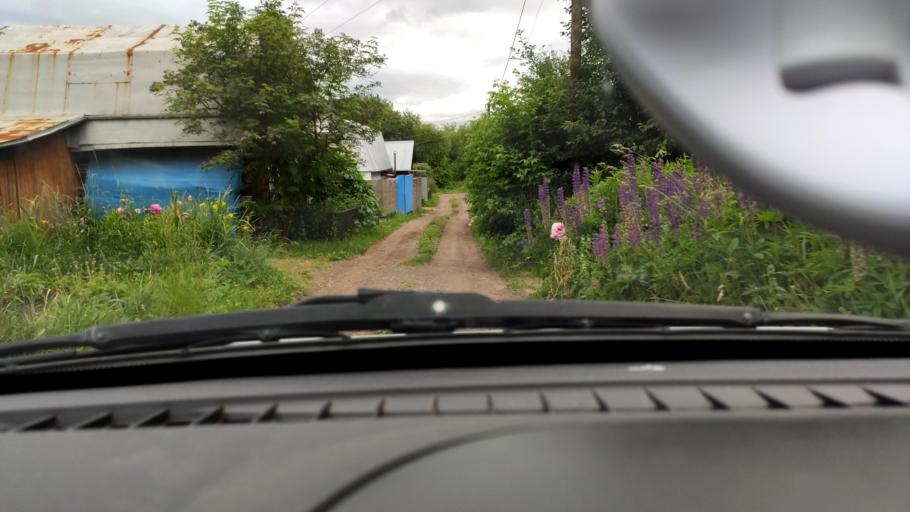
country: RU
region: Perm
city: Kondratovo
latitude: 57.9427
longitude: 56.1656
